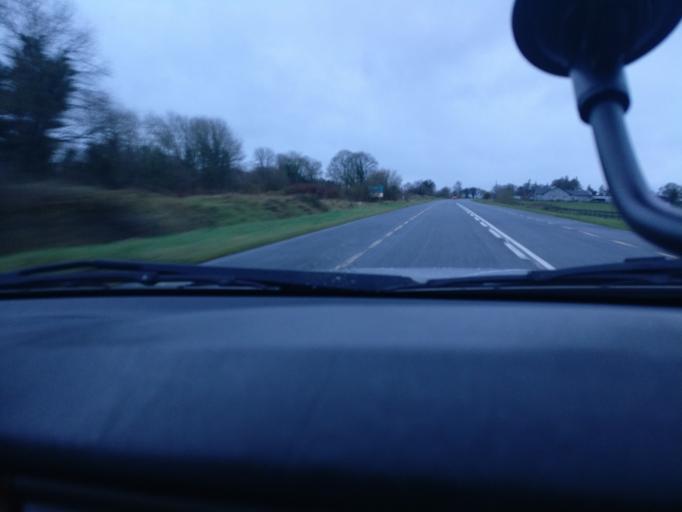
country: IE
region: Connaught
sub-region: County Galway
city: Ballinasloe
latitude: 53.2987
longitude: -8.3234
